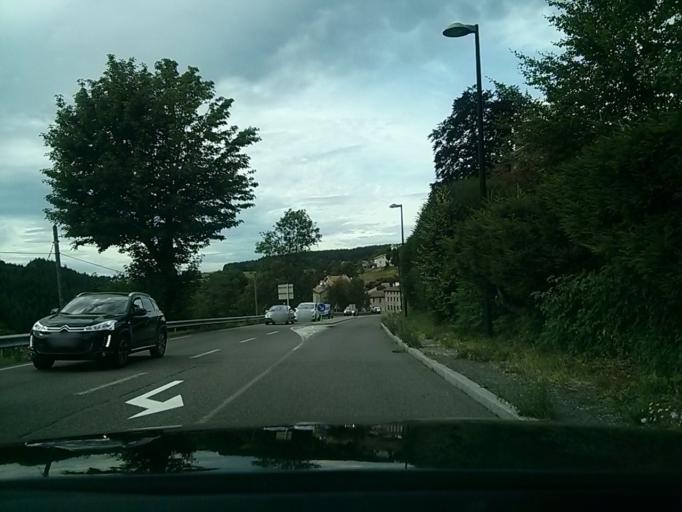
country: FR
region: Rhone-Alpes
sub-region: Departement de la Loire
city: Saint-Genest-Malifaux
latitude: 45.3809
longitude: 4.4389
